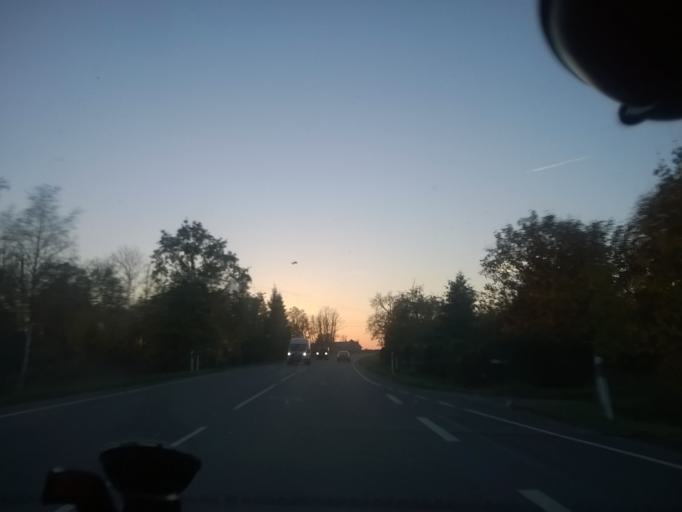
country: EE
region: Laeaene
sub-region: Ridala Parish
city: Uuemoisa
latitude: 58.9579
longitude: 23.8074
